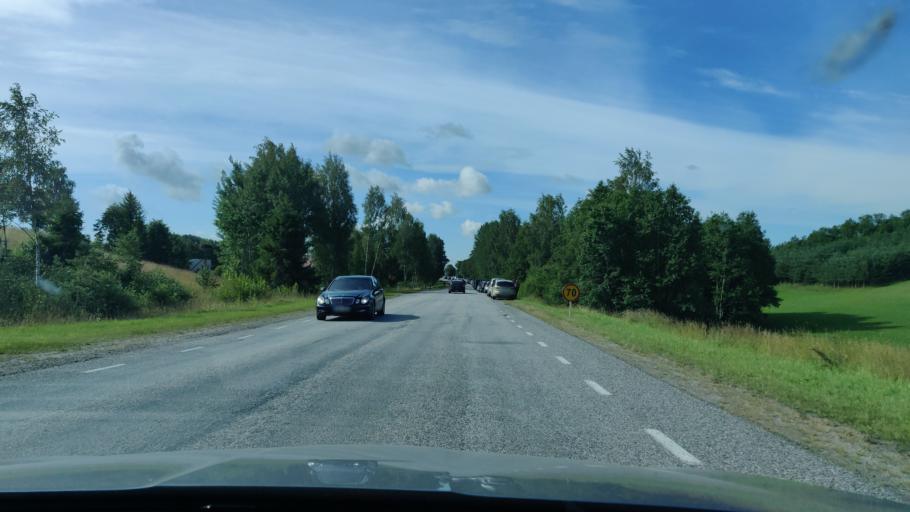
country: EE
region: Tartu
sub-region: Elva linn
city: Elva
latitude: 58.1428
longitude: 26.5225
